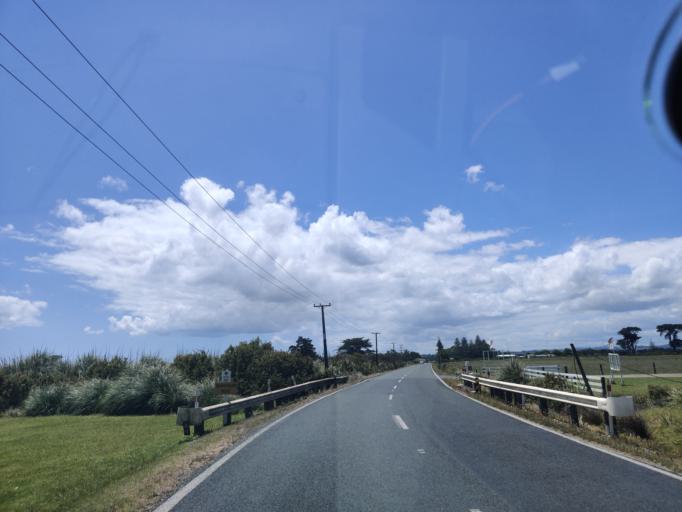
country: NZ
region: Northland
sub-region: Far North District
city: Kaitaia
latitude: -35.0247
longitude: 173.2299
